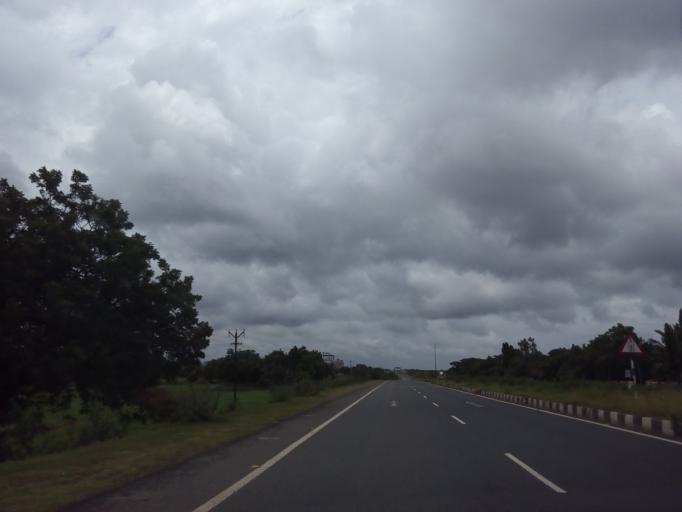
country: IN
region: Karnataka
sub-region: Haveri
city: Ranibennur
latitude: 14.6608
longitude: 75.5642
